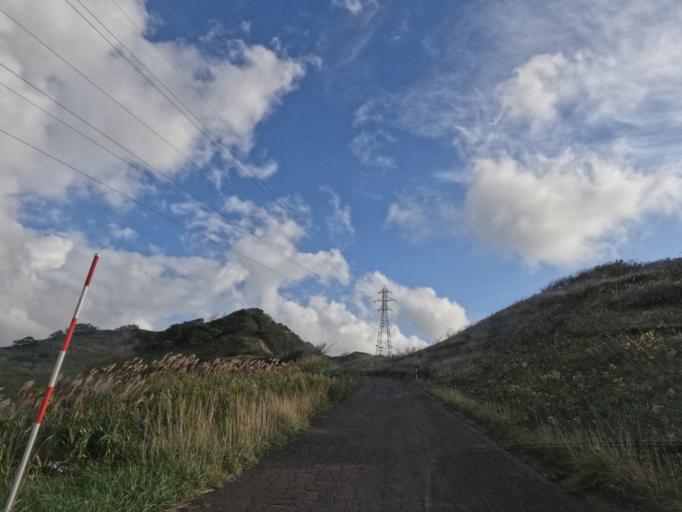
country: JP
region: Hokkaido
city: Muroran
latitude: 42.3092
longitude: 141.0052
